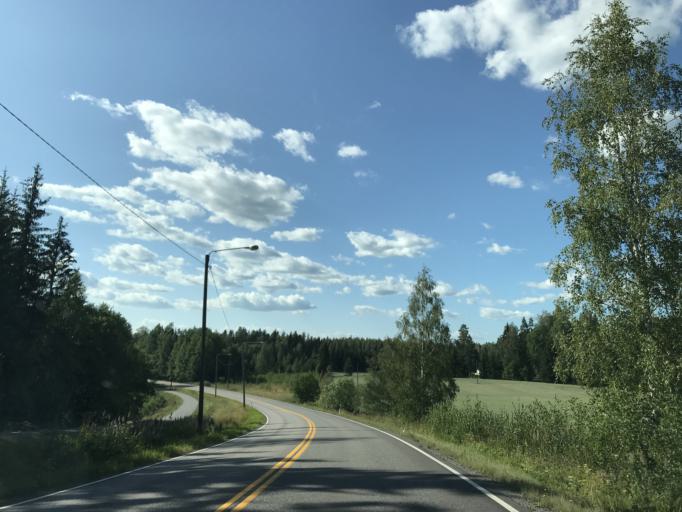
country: FI
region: Uusimaa
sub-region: Helsinki
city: Nurmijaervi
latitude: 60.4084
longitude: 24.8992
